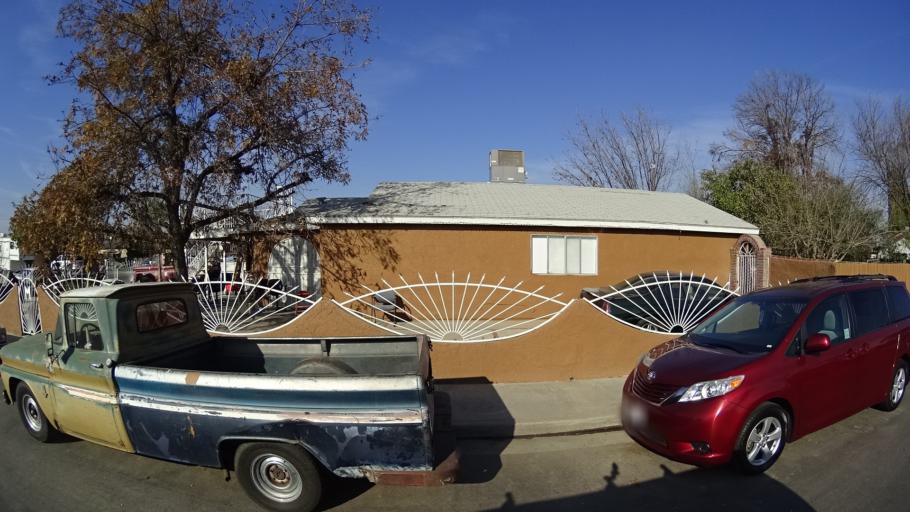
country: US
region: California
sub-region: Kern County
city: Greenfield
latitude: 35.3202
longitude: -119.0088
